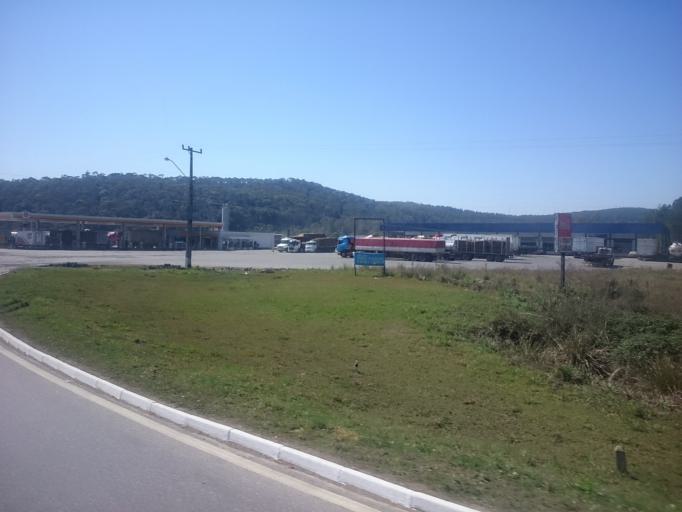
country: BR
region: Santa Catarina
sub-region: Santa Cecilia
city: Santa Cecilia
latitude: -26.7057
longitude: -50.2925
